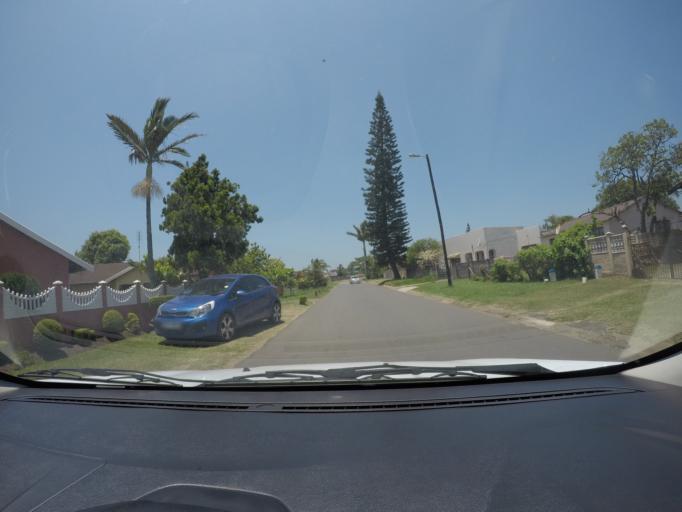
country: ZA
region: KwaZulu-Natal
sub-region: uThungulu District Municipality
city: eSikhawini
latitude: -28.8750
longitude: 31.8977
